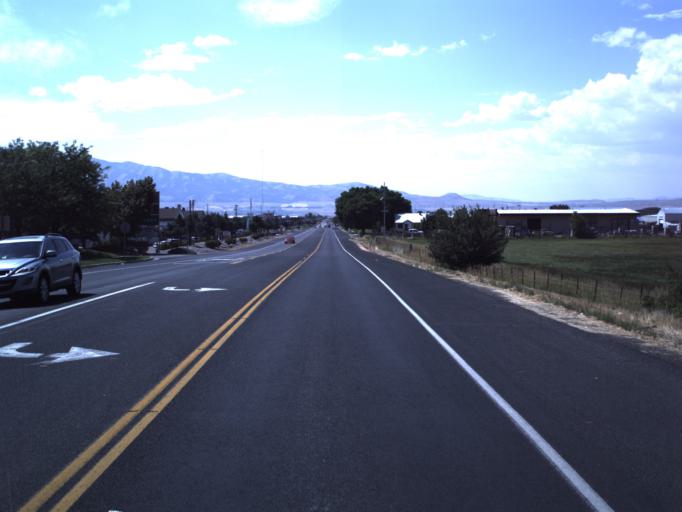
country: US
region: Utah
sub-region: Cache County
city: Logan
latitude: 41.7355
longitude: -111.8502
